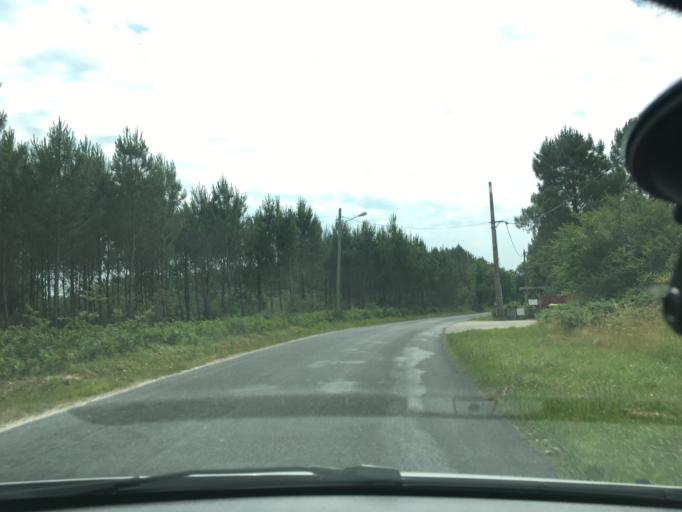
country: FR
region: Aquitaine
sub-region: Departement de la Gironde
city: Gaillan-en-Medoc
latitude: 45.3533
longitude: -1.0497
